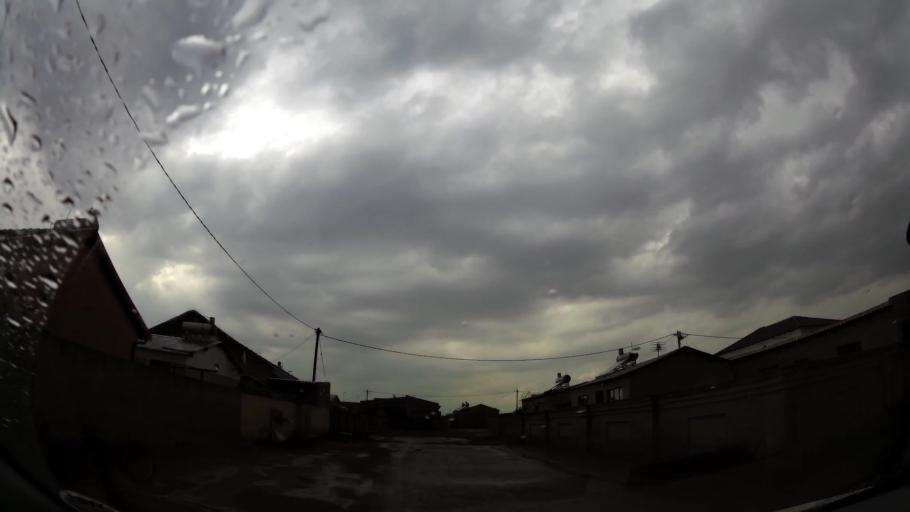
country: ZA
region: Gauteng
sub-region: Ekurhuleni Metropolitan Municipality
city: Germiston
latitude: -26.3738
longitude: 28.1495
